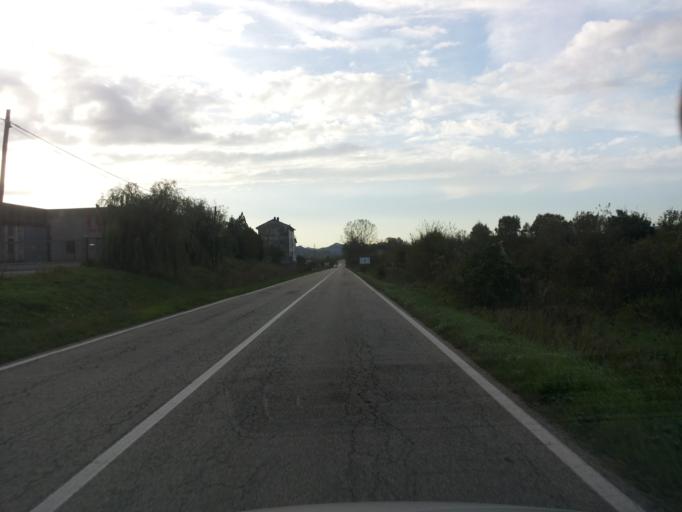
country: IT
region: Piedmont
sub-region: Provincia di Alessandria
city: Treville
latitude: 45.1077
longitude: 8.3492
